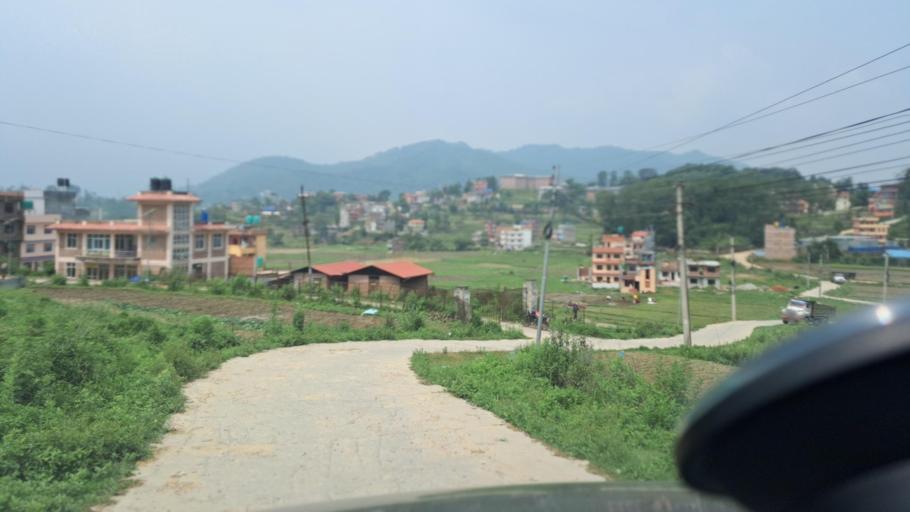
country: NP
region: Central Region
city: Banepa
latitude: 27.6181
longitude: 85.5463
